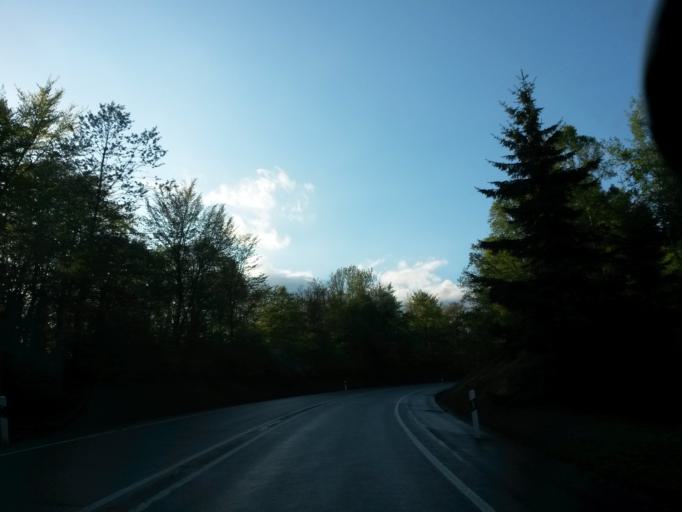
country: DE
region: North Rhine-Westphalia
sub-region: Regierungsbezirk Arnsberg
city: Herscheid
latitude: 51.1285
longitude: 7.7471
